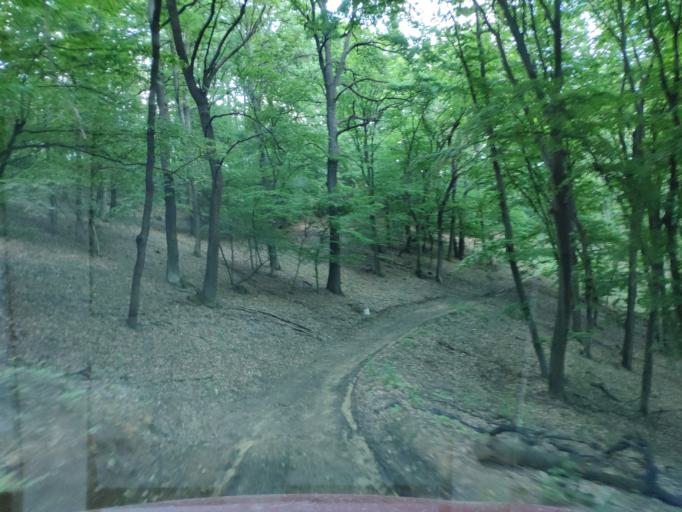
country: HU
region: Borsod-Abauj-Zemplen
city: Arlo
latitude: 48.2494
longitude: 20.1322
